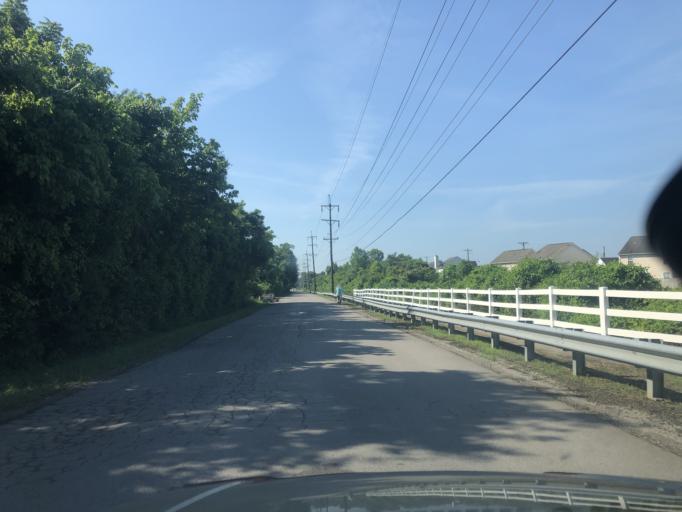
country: US
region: Tennessee
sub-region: Davidson County
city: Lakewood
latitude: 36.2433
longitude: -86.7018
